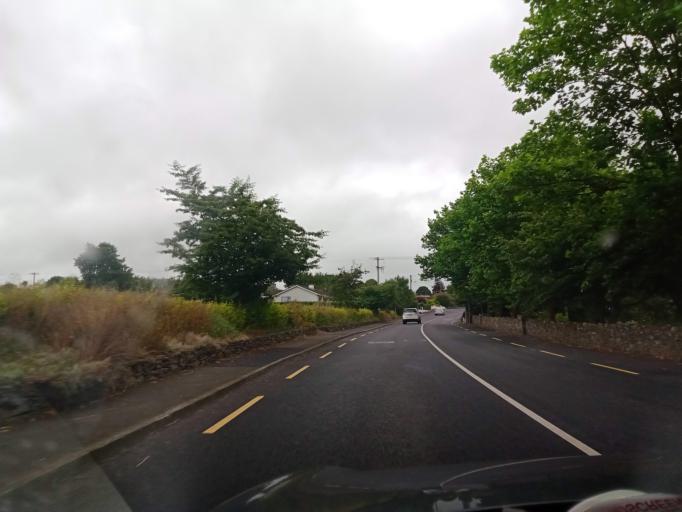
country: IE
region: Leinster
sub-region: Laois
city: Abbeyleix
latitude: 52.9110
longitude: -7.3331
